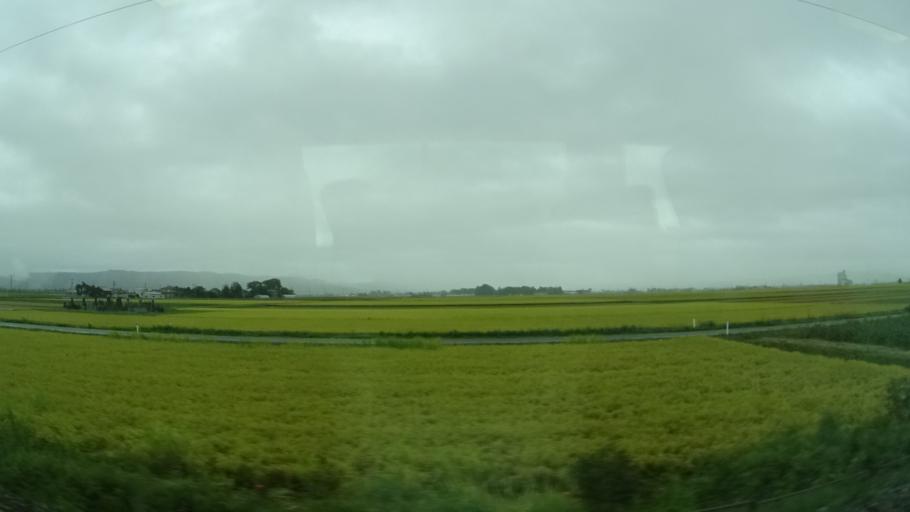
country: JP
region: Yamagata
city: Sakata
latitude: 38.8212
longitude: 139.9099
